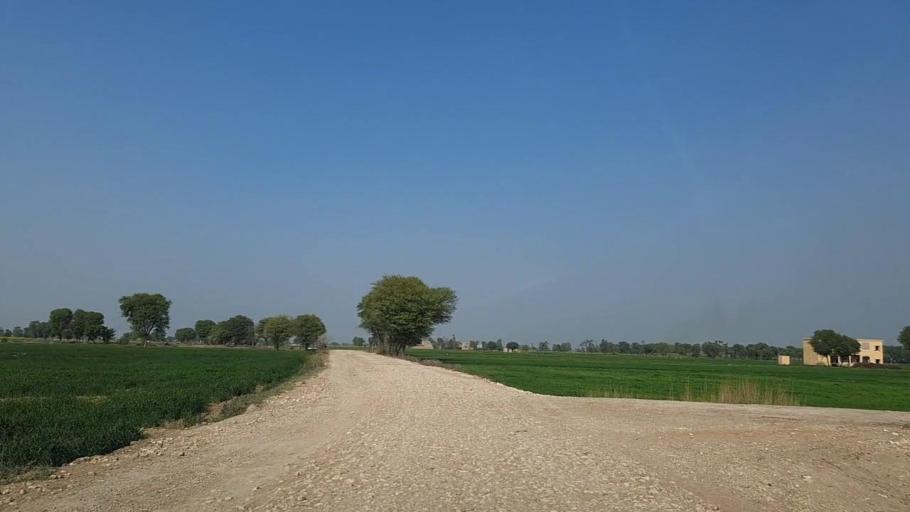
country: PK
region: Sindh
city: Moro
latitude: 26.6957
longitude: 67.9516
